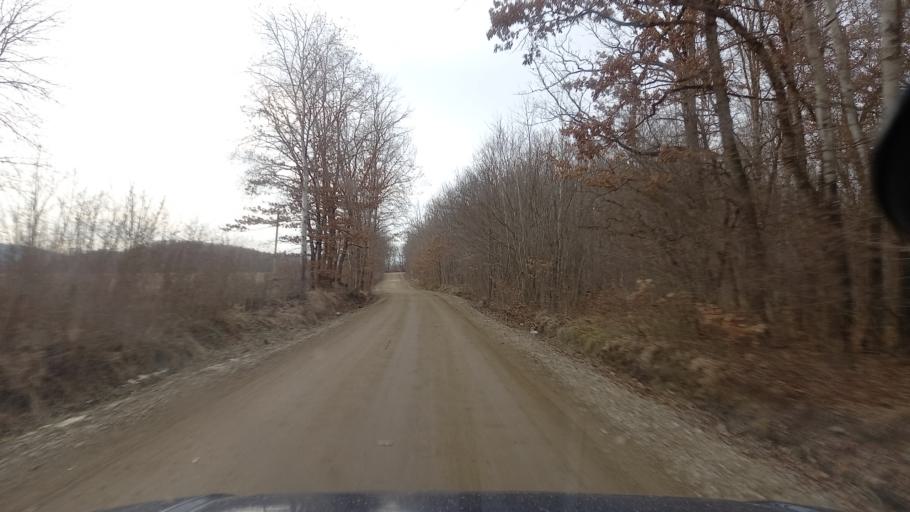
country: RU
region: Adygeya
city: Kamennomostskiy
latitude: 44.1391
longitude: 40.2611
